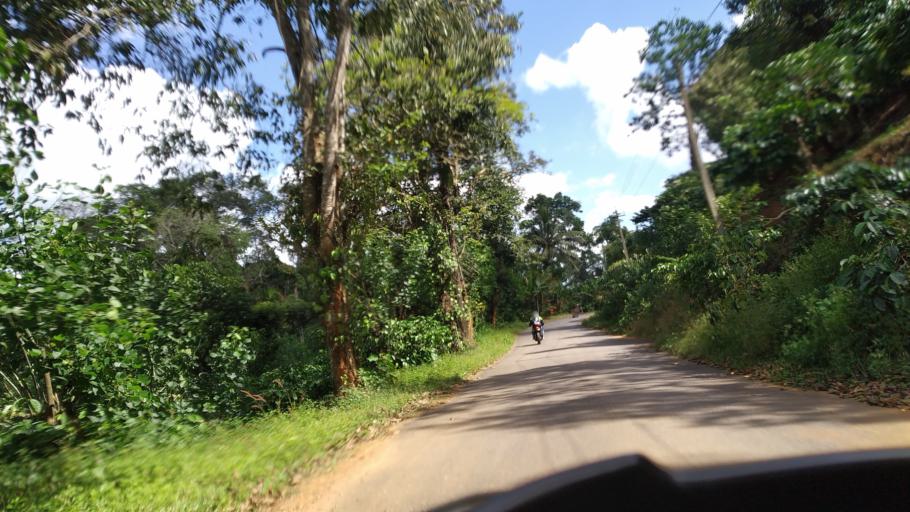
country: IN
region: Karnataka
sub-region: Kodagu
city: Ponnampet
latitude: 12.0362
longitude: 75.9171
